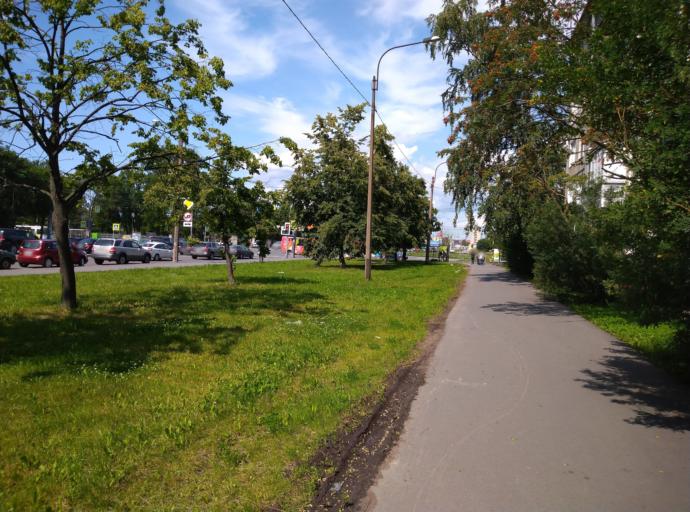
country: RU
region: St.-Petersburg
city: Kupchino
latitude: 59.8637
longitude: 30.3377
